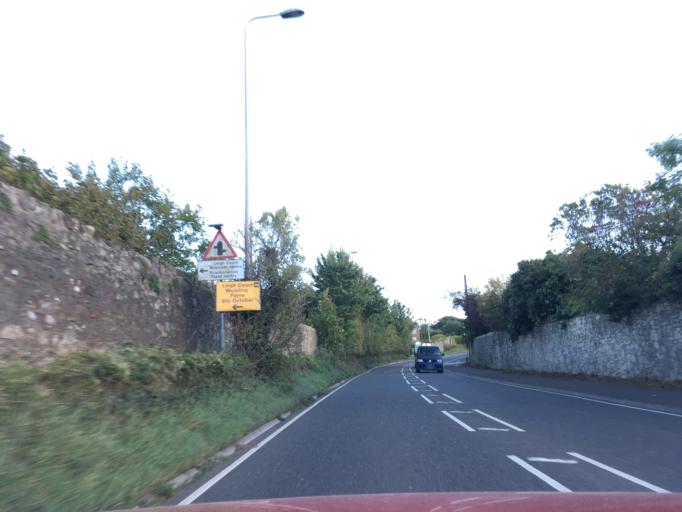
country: GB
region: England
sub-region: North Somerset
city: Easton-in-Gordano
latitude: 51.4640
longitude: -2.6677
